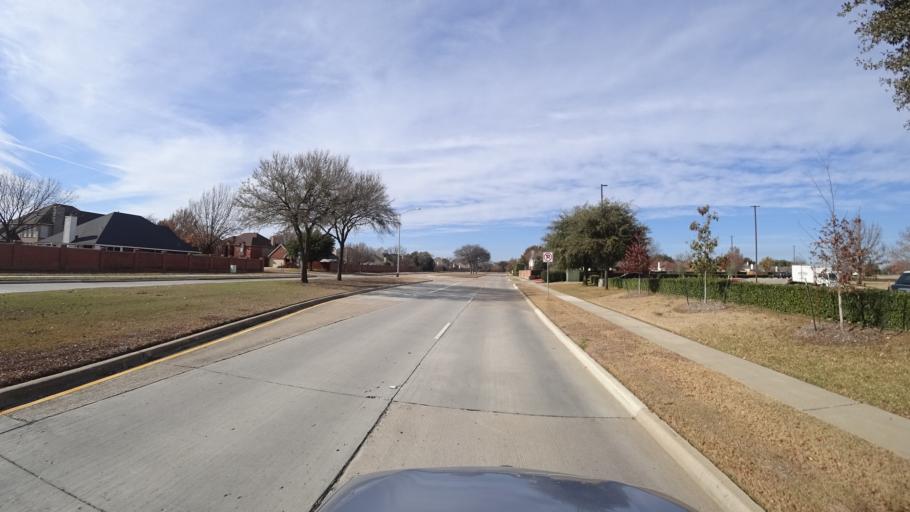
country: US
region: Texas
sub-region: Denton County
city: Lewisville
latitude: 33.0572
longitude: -97.0265
